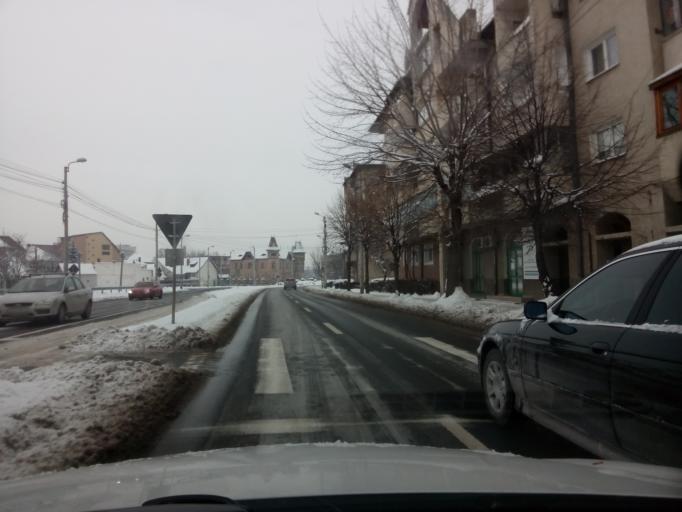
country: RO
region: Sibiu
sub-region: Municipiul Sibiu
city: Sibiu
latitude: 45.8001
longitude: 24.1572
